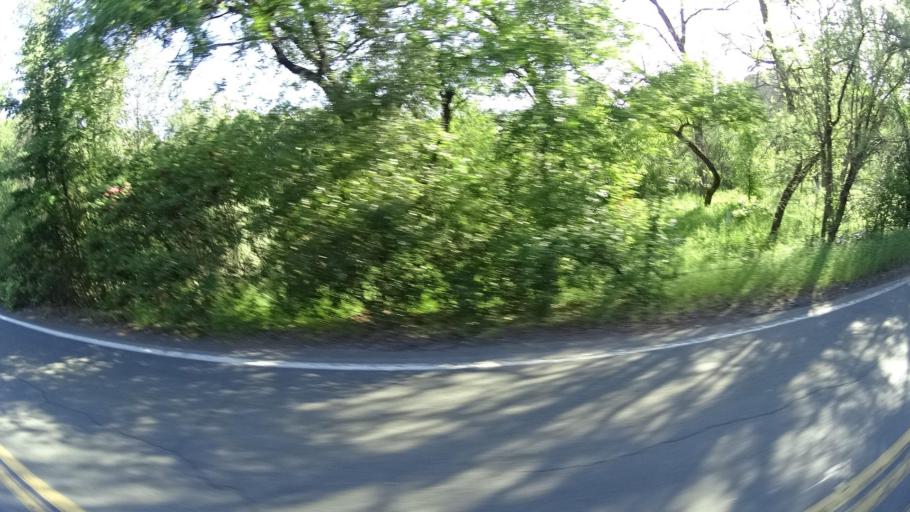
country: US
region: California
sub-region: Lake County
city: North Lakeport
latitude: 39.1112
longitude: -122.9776
